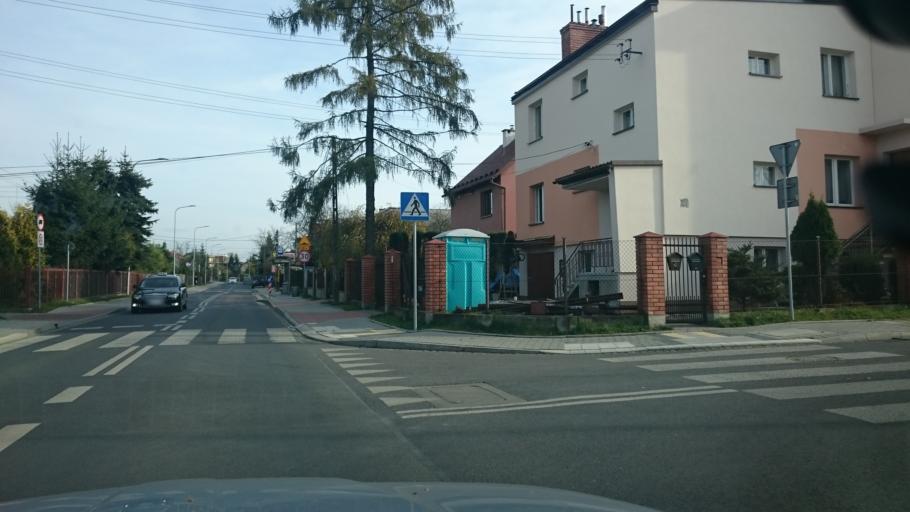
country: PL
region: Lesser Poland Voivodeship
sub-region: Powiat wielicki
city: Czarnochowice
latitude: 50.0212
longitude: 20.0165
